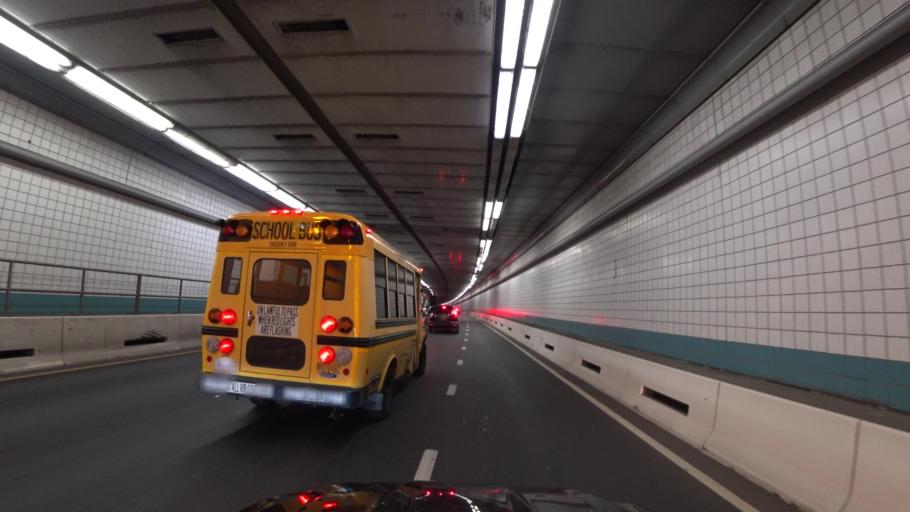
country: US
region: Massachusetts
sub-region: Suffolk County
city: South Boston
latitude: 42.3502
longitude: -71.0349
